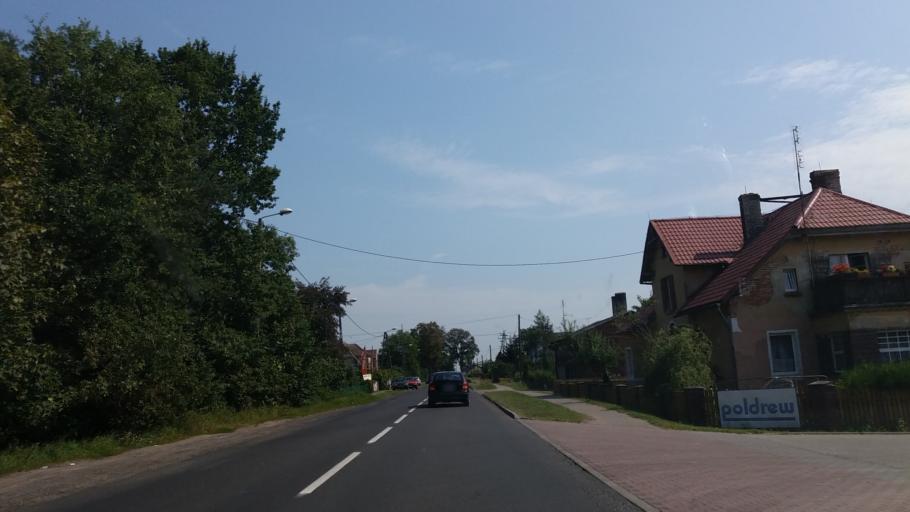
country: PL
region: Lubusz
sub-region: Powiat strzelecko-drezdenecki
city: Zwierzyn
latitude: 52.8384
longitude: 15.5752
